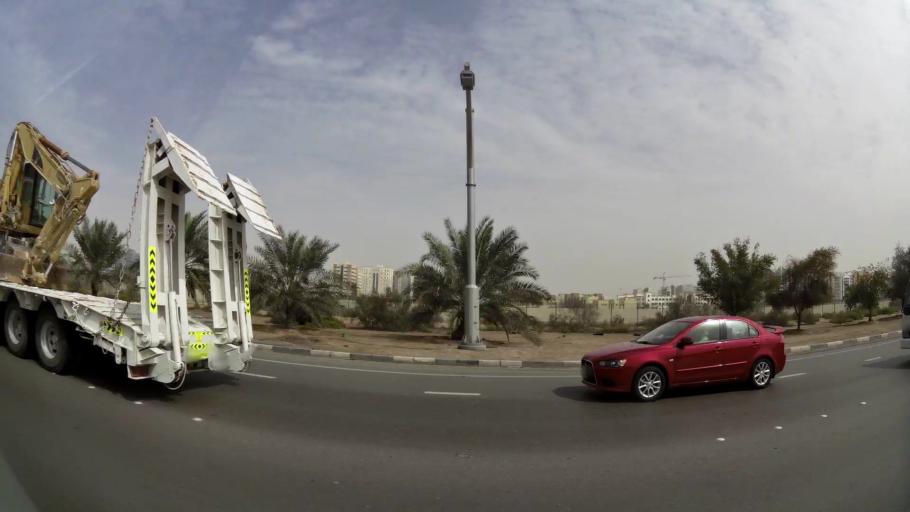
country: AE
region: Abu Dhabi
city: Abu Dhabi
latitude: 24.3402
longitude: 54.5266
